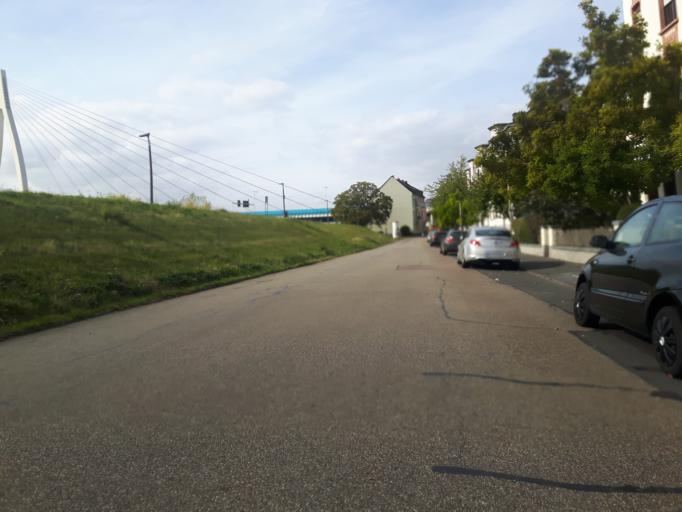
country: DE
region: Rheinland-Pfalz
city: Weissenthurm
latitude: 50.4214
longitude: 7.4632
